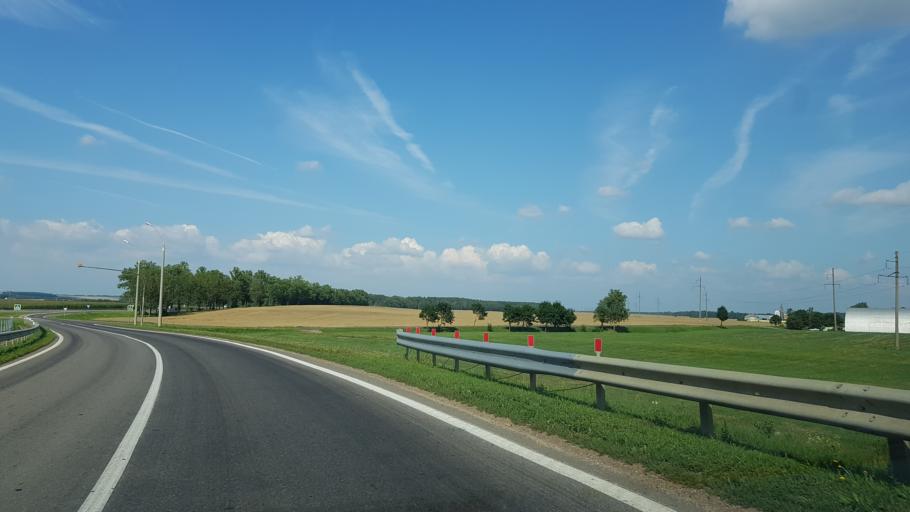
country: BY
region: Minsk
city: Stan'kava
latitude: 53.7050
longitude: 27.2187
